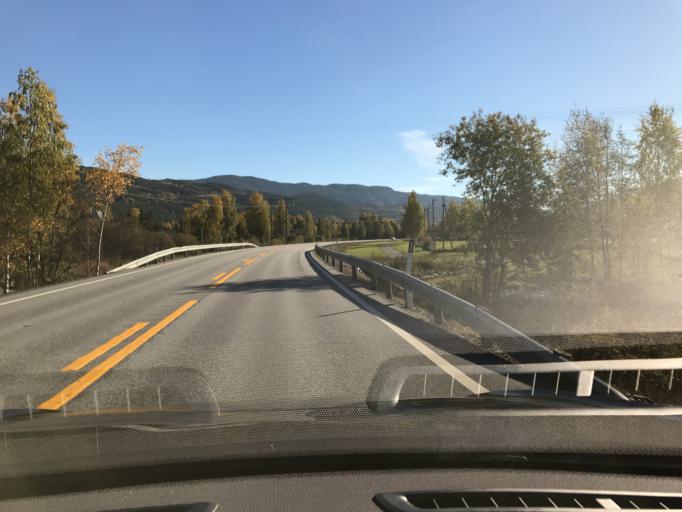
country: NO
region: Buskerud
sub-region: Nes
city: Nesbyen
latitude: 60.5753
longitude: 9.1070
